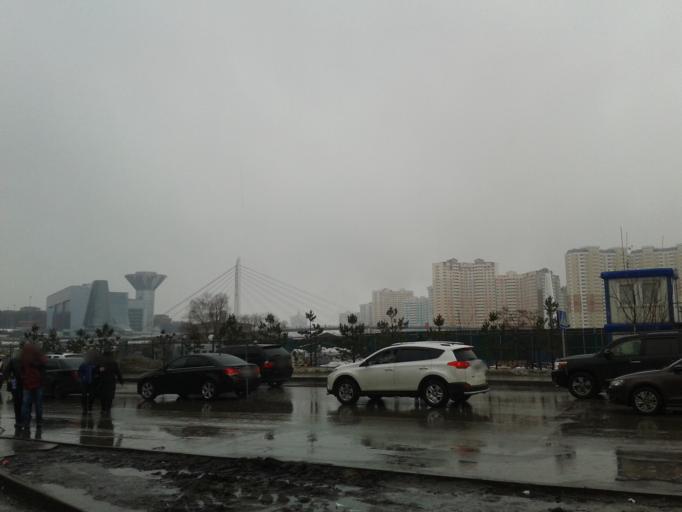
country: RU
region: Moscow
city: Strogino
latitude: 55.8229
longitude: 37.3852
